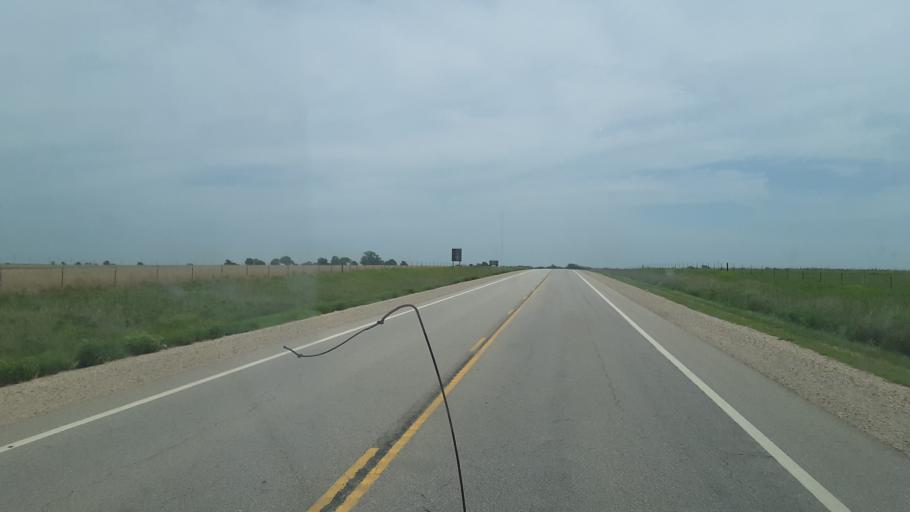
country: US
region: Kansas
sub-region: Greenwood County
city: Eureka
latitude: 37.8174
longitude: -96.2508
